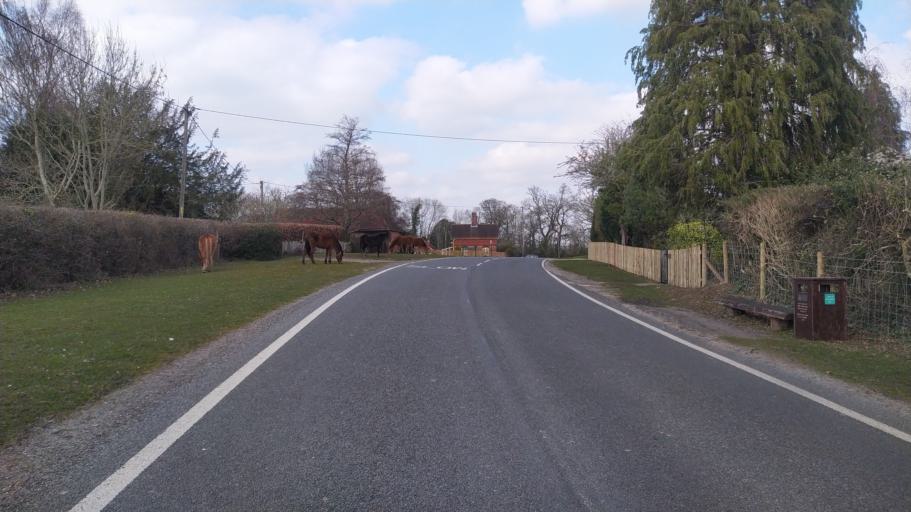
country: GB
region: England
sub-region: Hampshire
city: Cadnam
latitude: 50.9370
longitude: -1.6173
